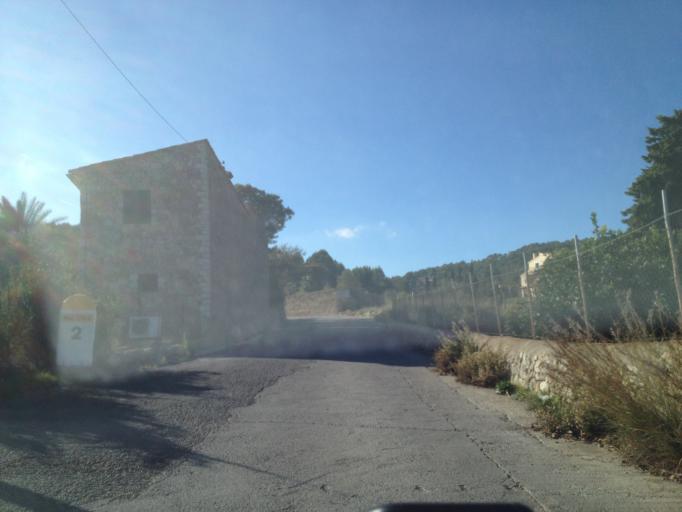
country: ES
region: Balearic Islands
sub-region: Illes Balears
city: Selva
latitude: 39.7511
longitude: 2.9008
